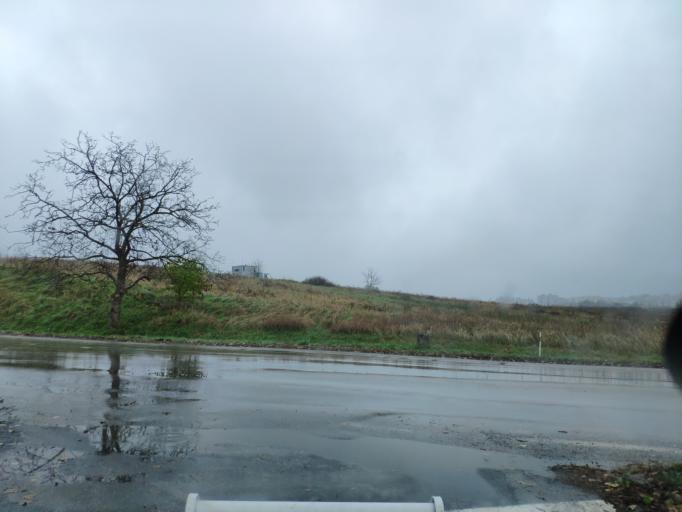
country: HU
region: Borsod-Abauj-Zemplen
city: Ricse
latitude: 48.4300
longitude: 21.9833
